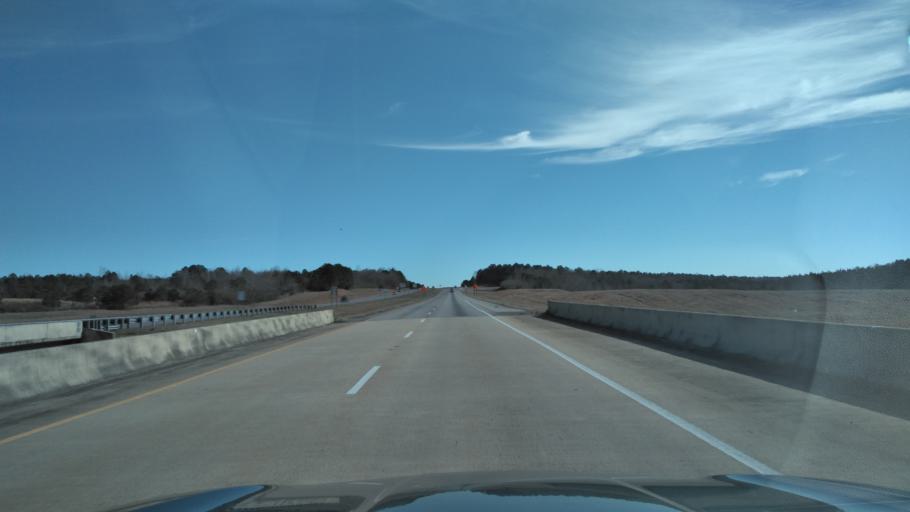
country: US
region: Alabama
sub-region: Walker County
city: Carbon Hill
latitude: 33.9111
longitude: -87.5031
